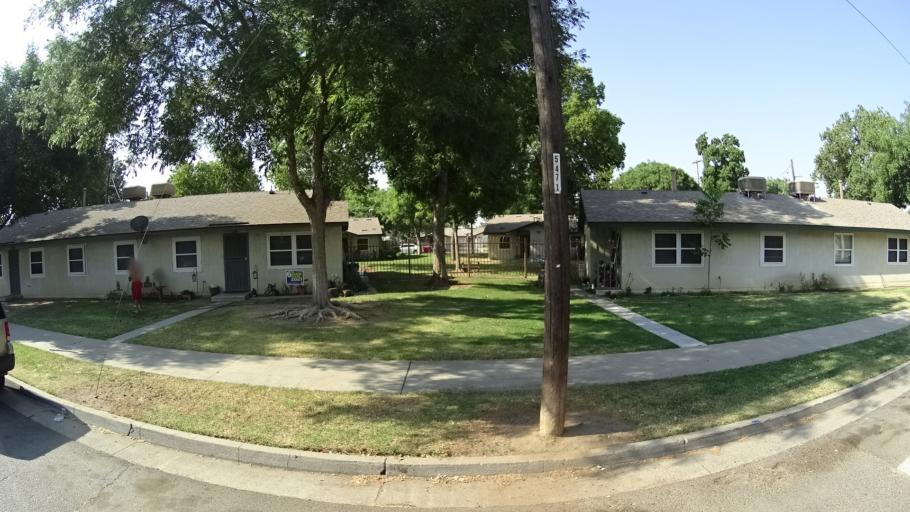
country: US
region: California
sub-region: Fresno County
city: Fresno
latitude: 36.7380
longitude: -119.8107
